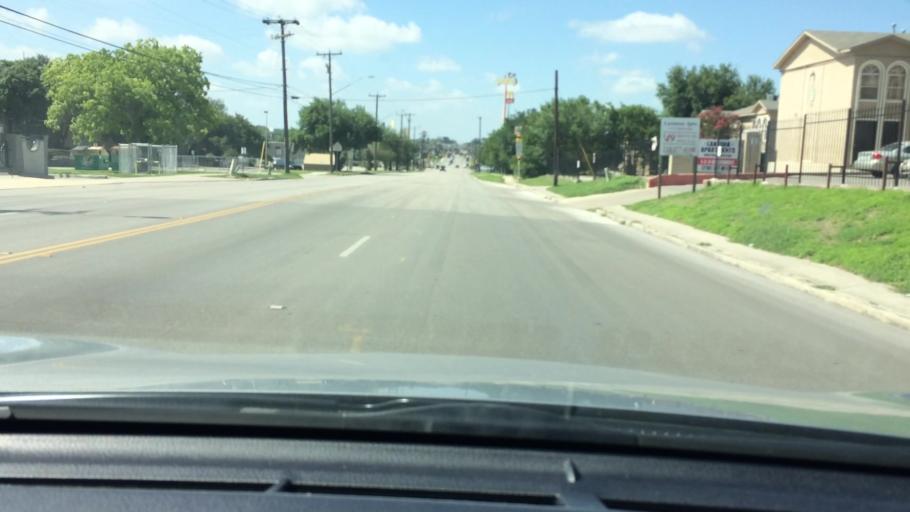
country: US
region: Texas
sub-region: Bexar County
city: Castle Hills
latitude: 29.5180
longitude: -98.5352
